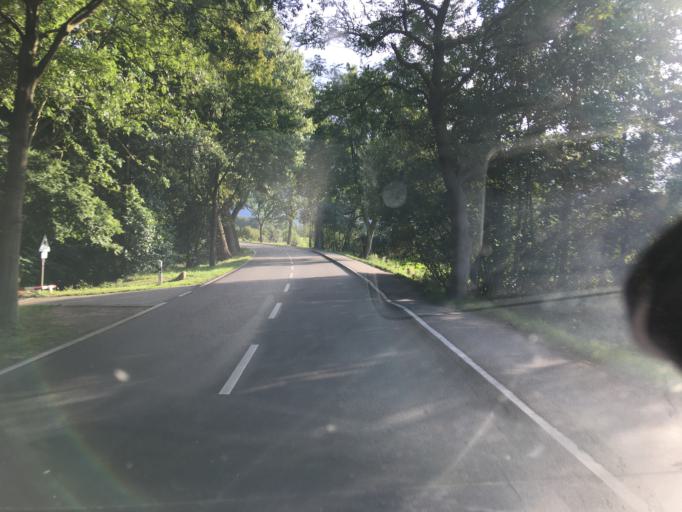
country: DE
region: Lower Saxony
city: Neu Wulmstorf
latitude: 53.4894
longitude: 9.8690
